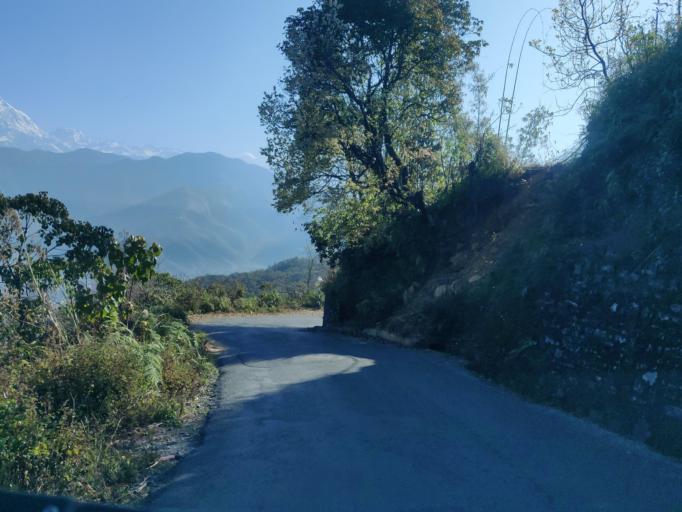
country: NP
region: Western Region
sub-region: Gandaki Zone
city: Pokhara
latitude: 28.2443
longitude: 83.9578
